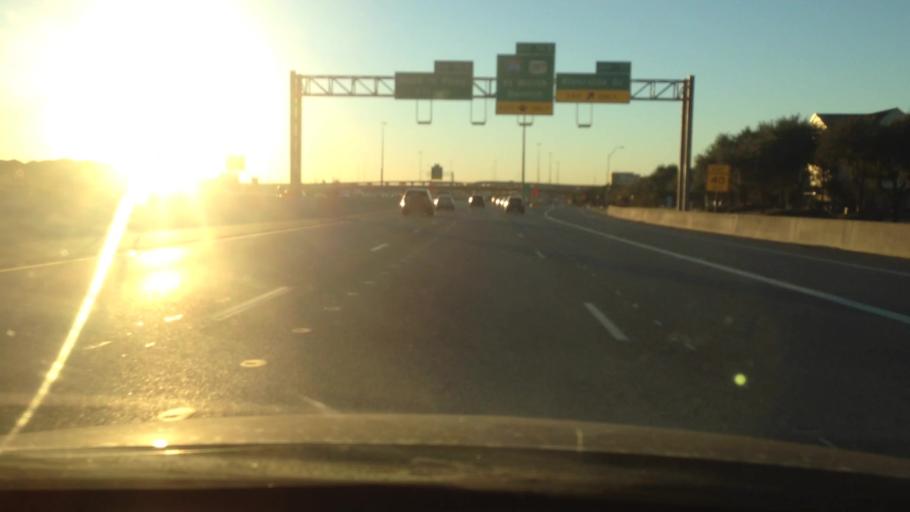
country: US
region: Texas
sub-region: Tarrant County
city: Watauga
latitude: 32.8397
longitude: -97.2937
